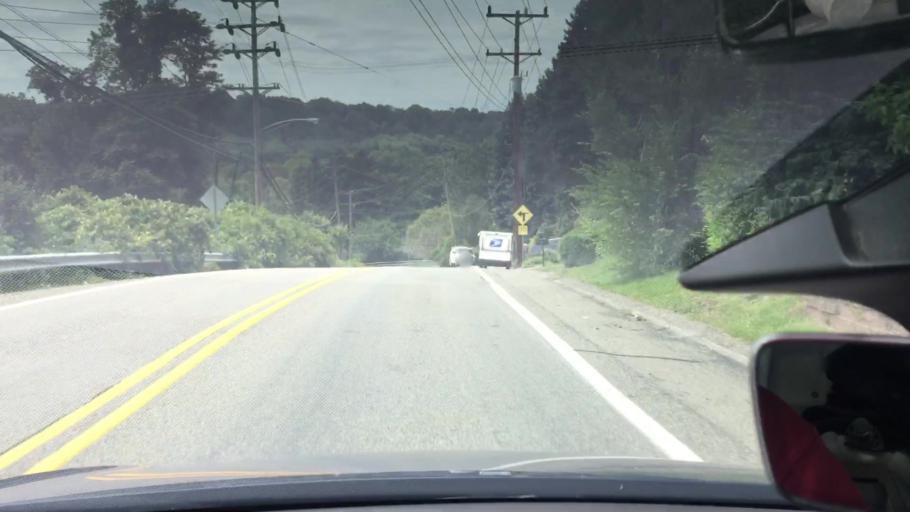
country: US
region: Pennsylvania
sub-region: Allegheny County
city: Monroeville
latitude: 40.4468
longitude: -79.7984
